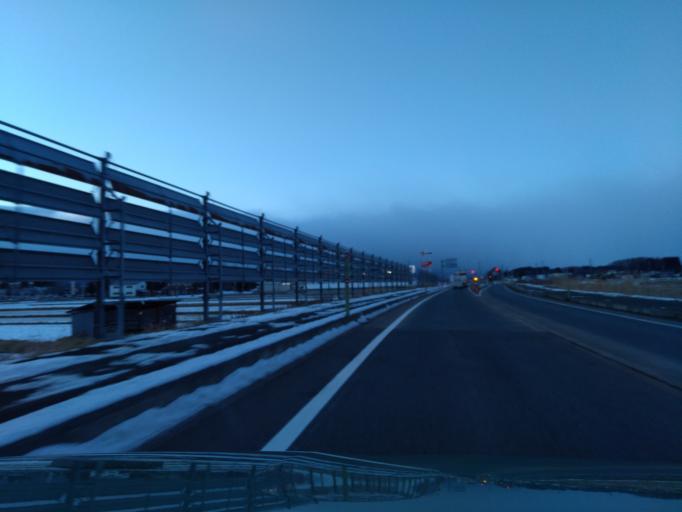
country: JP
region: Iwate
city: Shizukuishi
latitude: 39.6940
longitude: 140.9805
